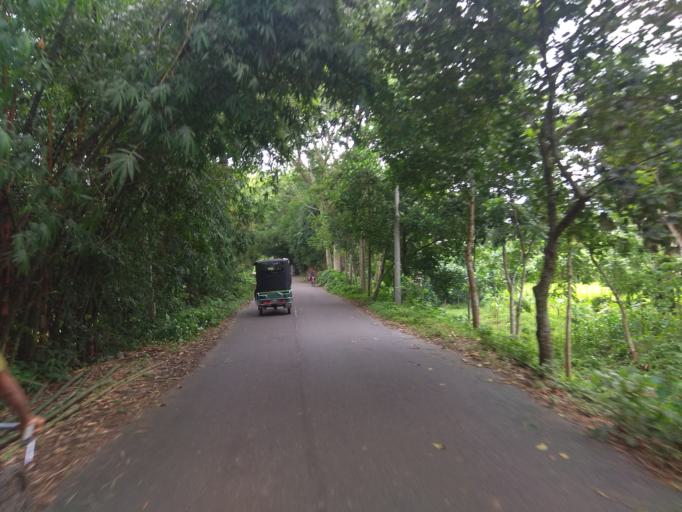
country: BD
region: Dhaka
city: Dohar
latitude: 23.4449
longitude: 90.0635
